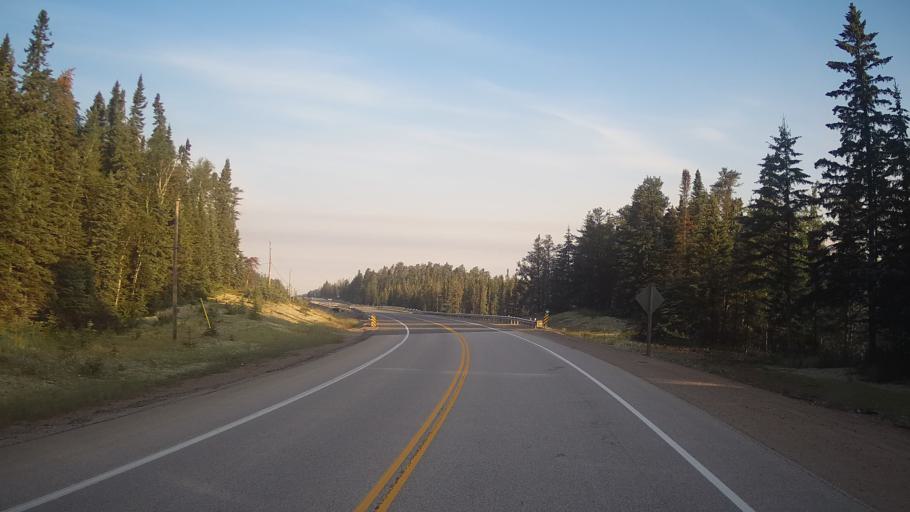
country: CA
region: Ontario
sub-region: Rainy River District
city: Atikokan
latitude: 49.2329
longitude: -90.9684
